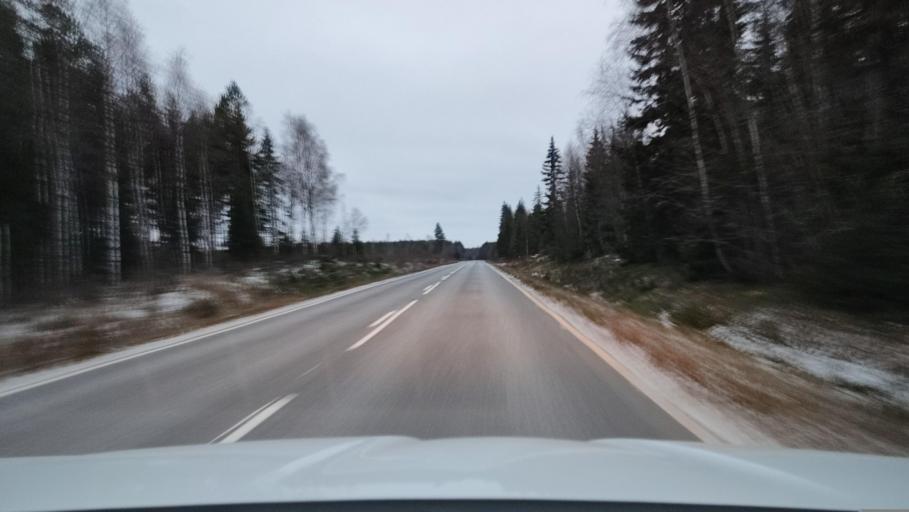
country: FI
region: Ostrobothnia
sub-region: Vaasa
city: Replot
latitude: 63.2458
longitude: 21.3794
